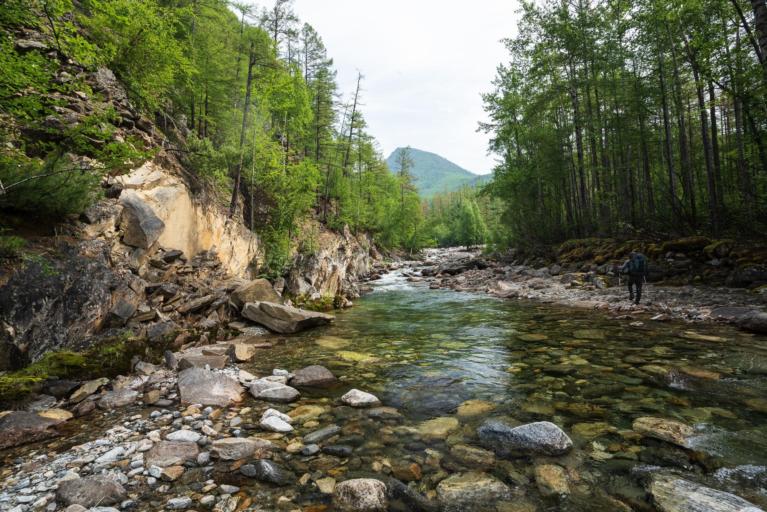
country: RU
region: Transbaikal Territory
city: Kuanda
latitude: 56.6654
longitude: 116.4341
